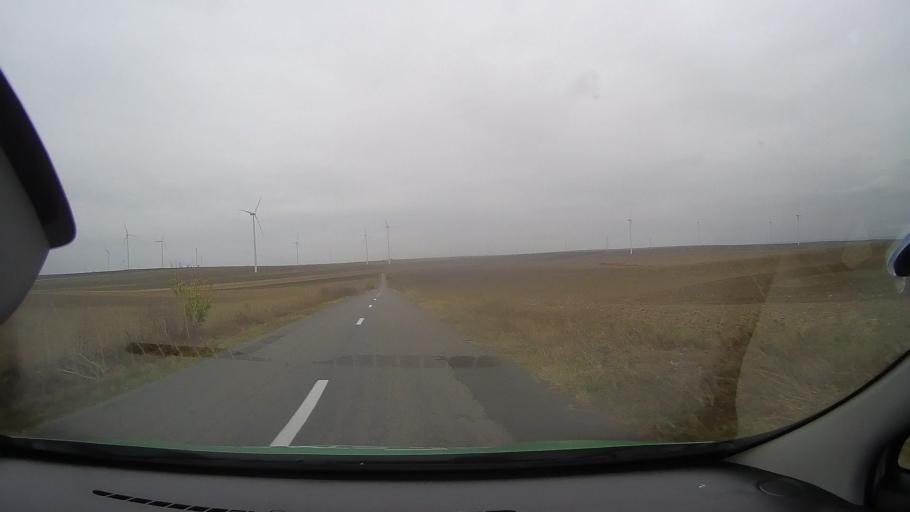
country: RO
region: Constanta
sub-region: Comuna Pantelimon
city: Pantelimon
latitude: 44.5120
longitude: 28.3367
